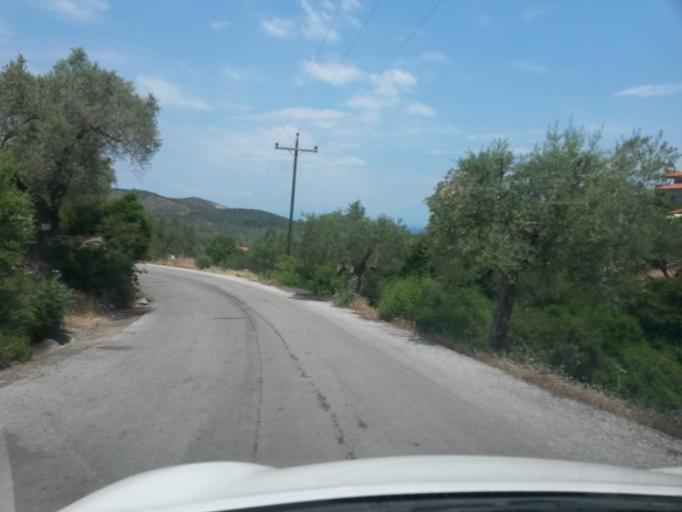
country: GR
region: North Aegean
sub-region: Nomos Lesvou
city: Pamfylla
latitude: 39.1776
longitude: 26.4824
